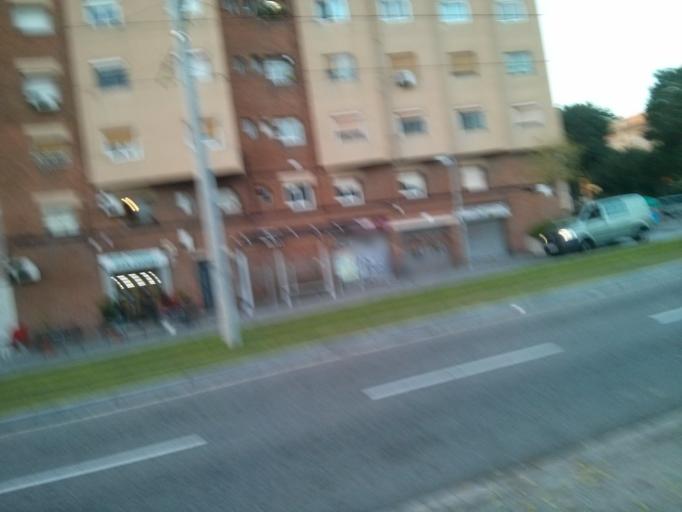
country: ES
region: Catalonia
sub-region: Provincia de Barcelona
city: Esplugues de Llobregat
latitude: 41.3763
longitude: 2.1036
